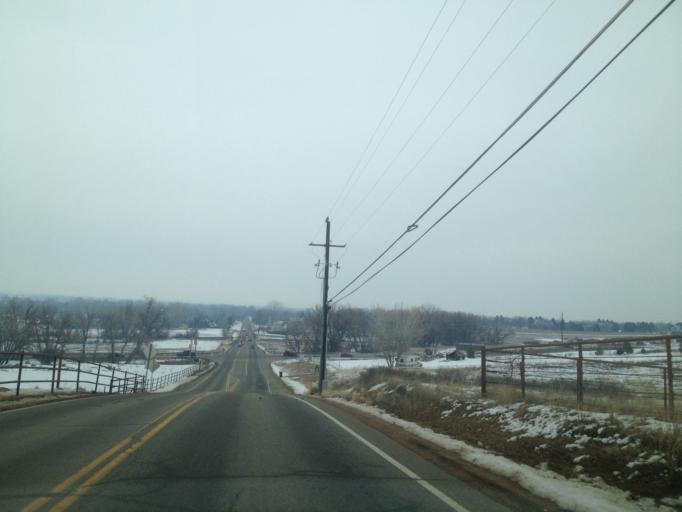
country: US
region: Colorado
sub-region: Boulder County
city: Niwot
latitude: 40.0852
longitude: -105.1691
